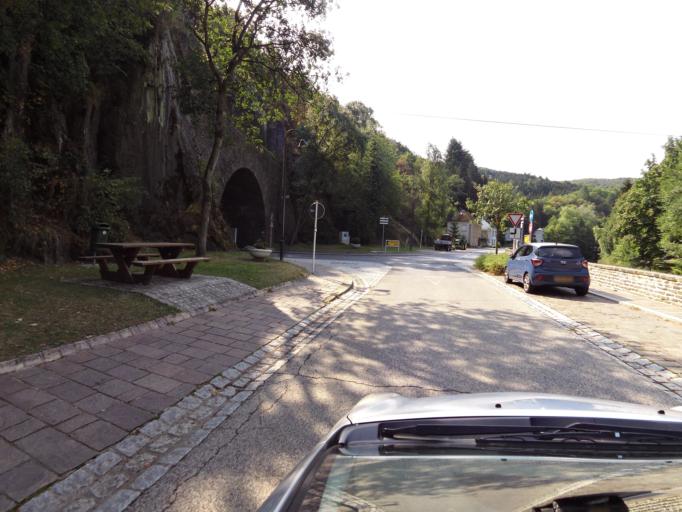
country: LU
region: Diekirch
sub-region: Canton de Wiltz
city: Esch-sur-Sure
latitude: 49.9101
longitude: 5.9341
